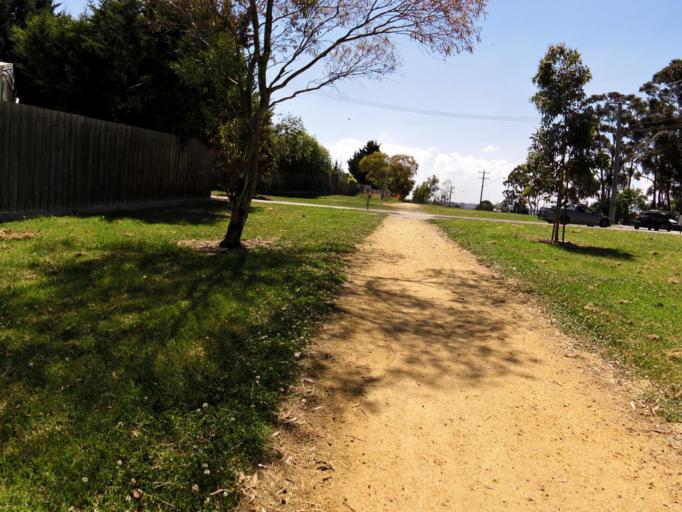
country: AU
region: Victoria
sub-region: Casey
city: Narre Warren South
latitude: -38.0316
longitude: 145.2813
